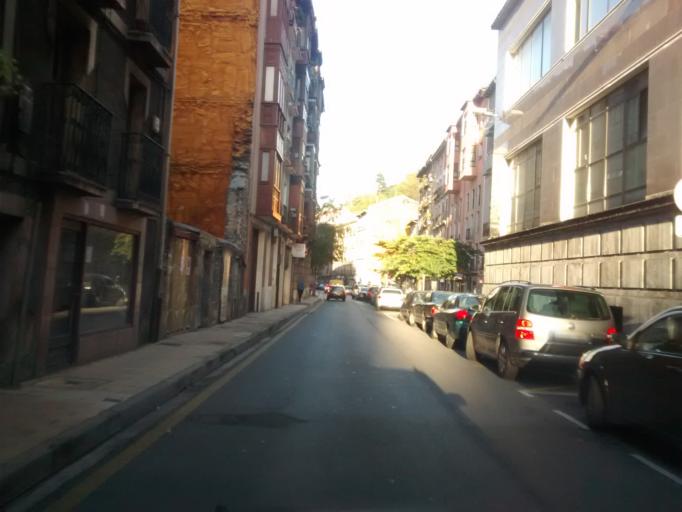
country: ES
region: Basque Country
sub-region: Provincia de Guipuzcoa
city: Eibar
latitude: 43.1854
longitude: -2.4658
